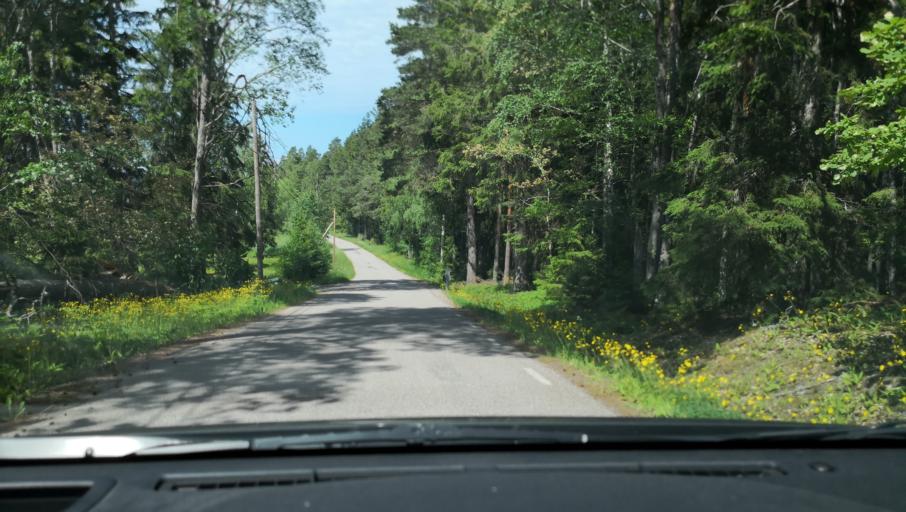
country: SE
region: Stockholm
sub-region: Sigtuna Kommun
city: Sigtuna
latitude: 59.6947
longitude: 17.6440
